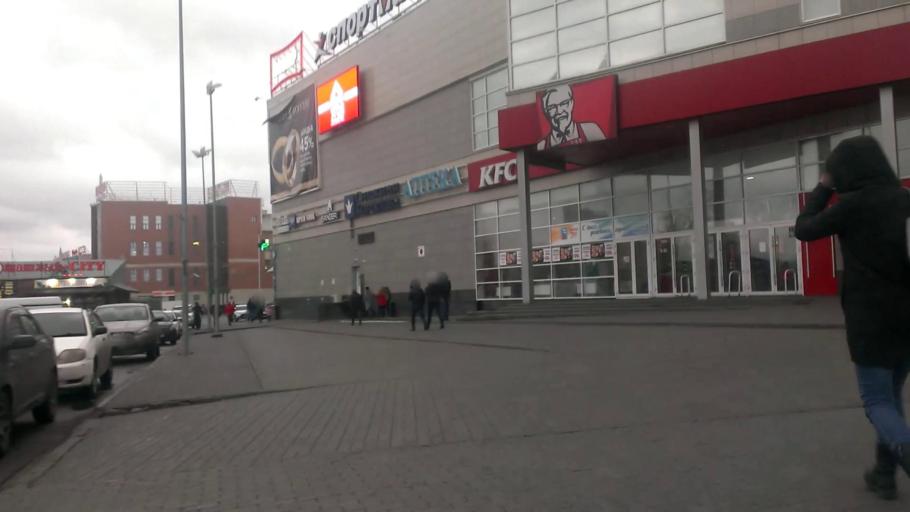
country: RU
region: Altai Krai
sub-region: Gorod Barnaulskiy
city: Barnaul
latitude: 53.3591
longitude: 83.6987
